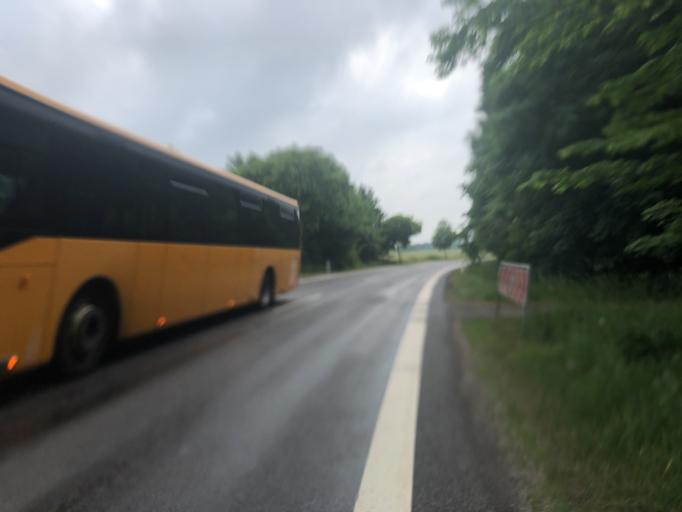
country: DK
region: Capital Region
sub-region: Bornholm Kommune
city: Akirkeby
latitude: 55.1518
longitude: 14.8902
